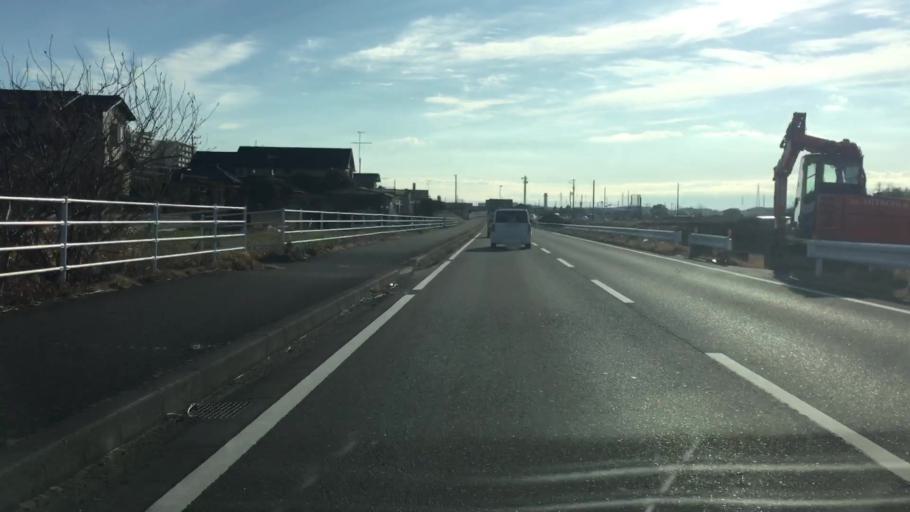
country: JP
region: Ibaraki
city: Toride
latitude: 35.8500
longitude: 140.1278
